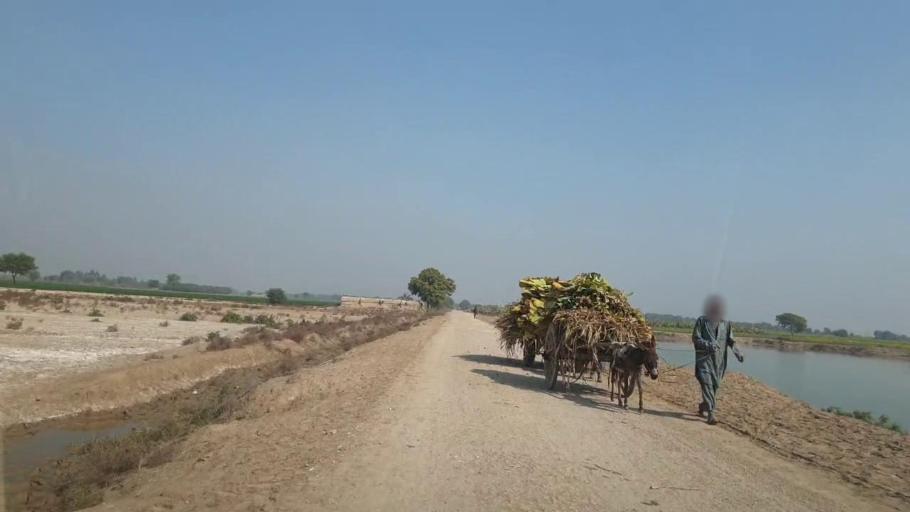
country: PK
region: Sindh
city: Matiari
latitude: 25.5362
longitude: 68.4715
